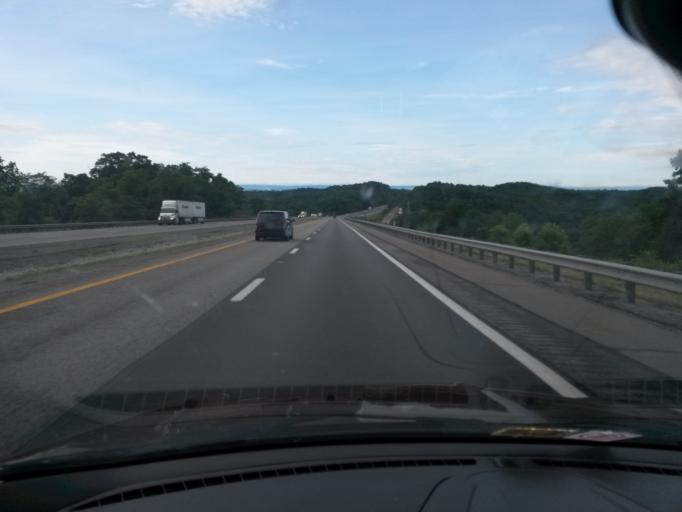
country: US
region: West Virginia
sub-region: Raleigh County
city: Shady Spring
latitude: 37.5604
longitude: -81.1138
